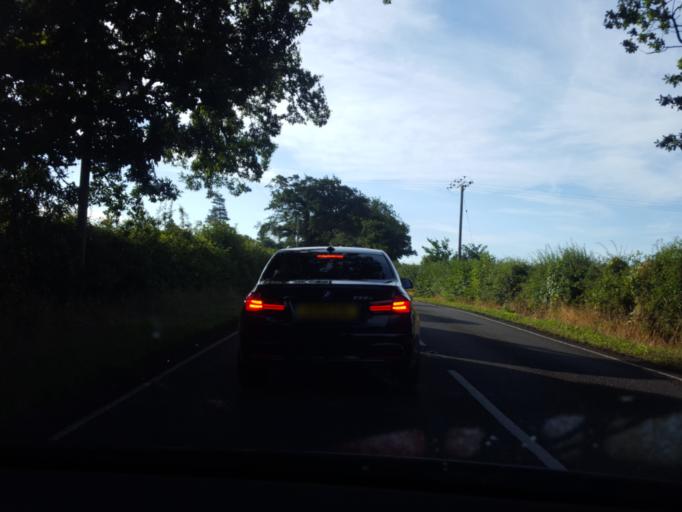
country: GB
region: England
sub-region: Leicestershire
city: Shepshed
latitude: 52.7422
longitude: -1.2709
